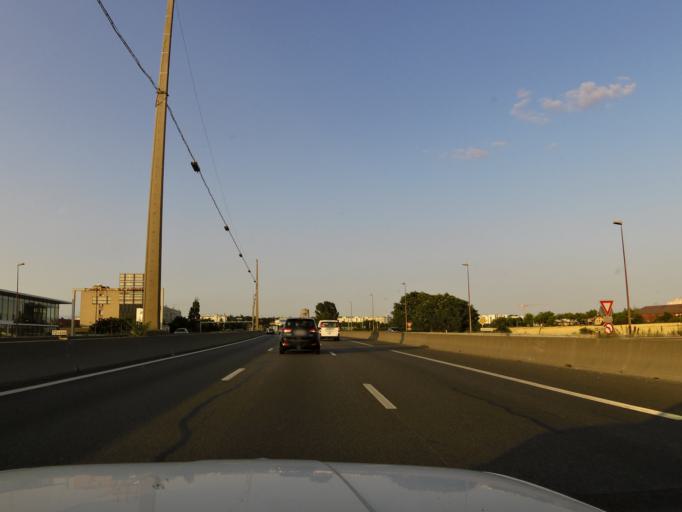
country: FR
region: Rhone-Alpes
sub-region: Departement du Rhone
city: Venissieux
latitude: 45.7193
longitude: 4.8782
